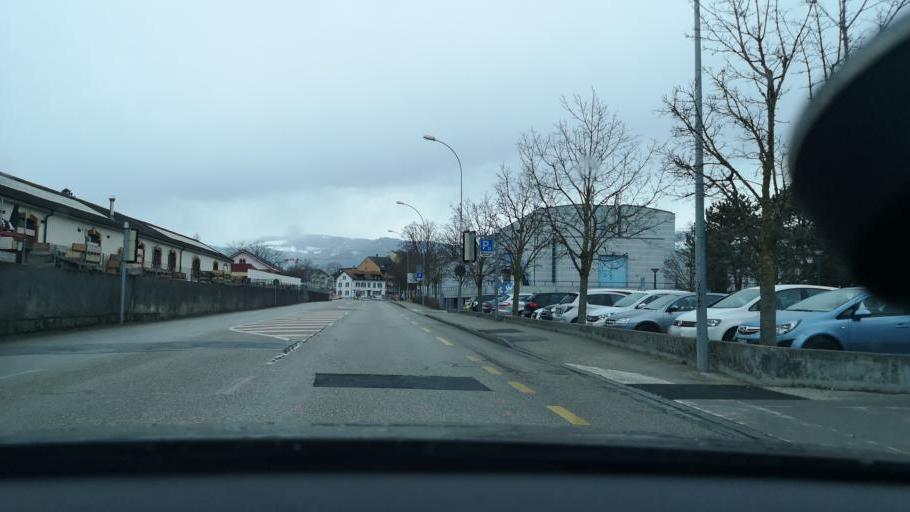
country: CH
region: Vaud
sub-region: Jura-Nord vaudois District
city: Yverdon-les-Bains
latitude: 46.7847
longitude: 6.6396
